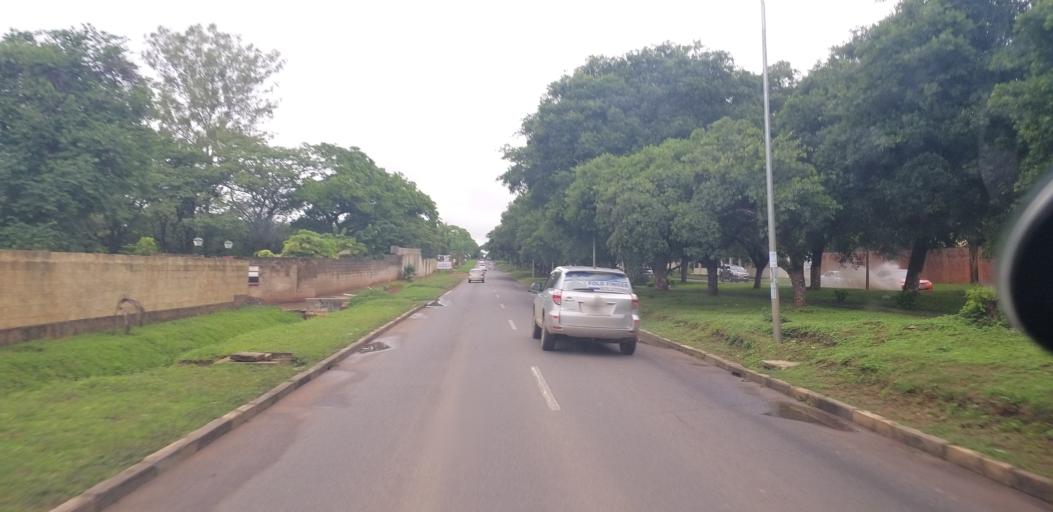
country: ZM
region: Lusaka
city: Lusaka
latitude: -15.4263
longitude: 28.3154
